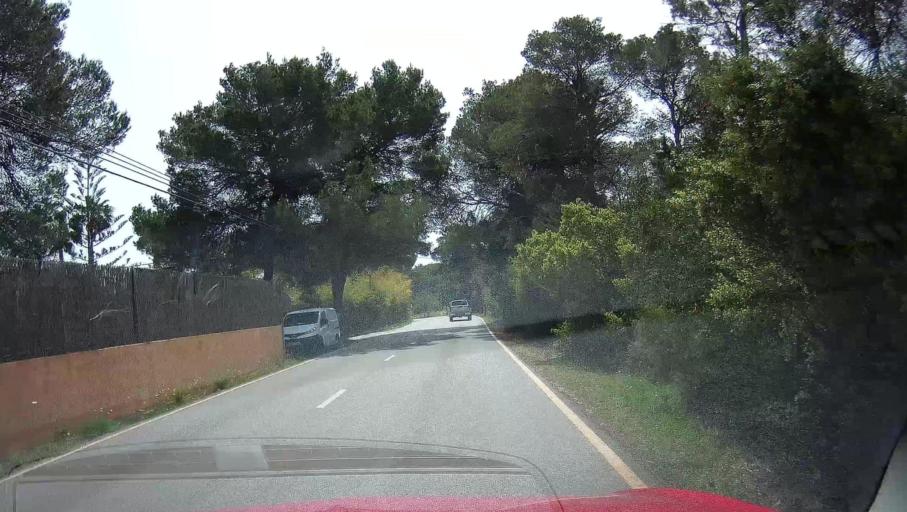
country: ES
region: Balearic Islands
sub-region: Illes Balears
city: Santa Eularia des Riu
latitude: 39.0091
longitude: 1.5690
